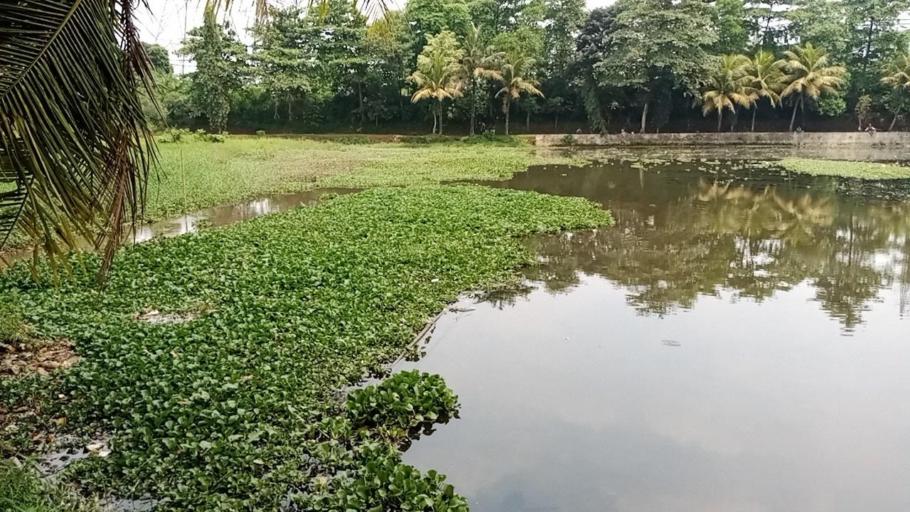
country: ID
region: West Java
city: Sawangan
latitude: -6.4133
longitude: 106.7957
